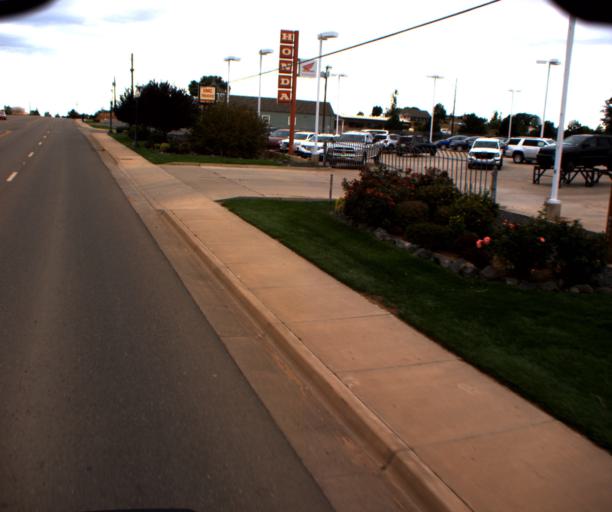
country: US
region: Arizona
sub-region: Navajo County
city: Snowflake
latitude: 34.4978
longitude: -110.0791
